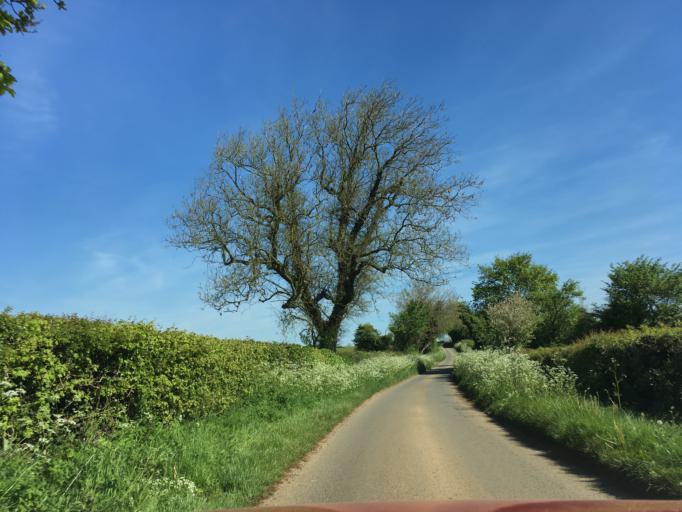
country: GB
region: England
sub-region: Wiltshire
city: Luckington
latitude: 51.5996
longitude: -2.2561
